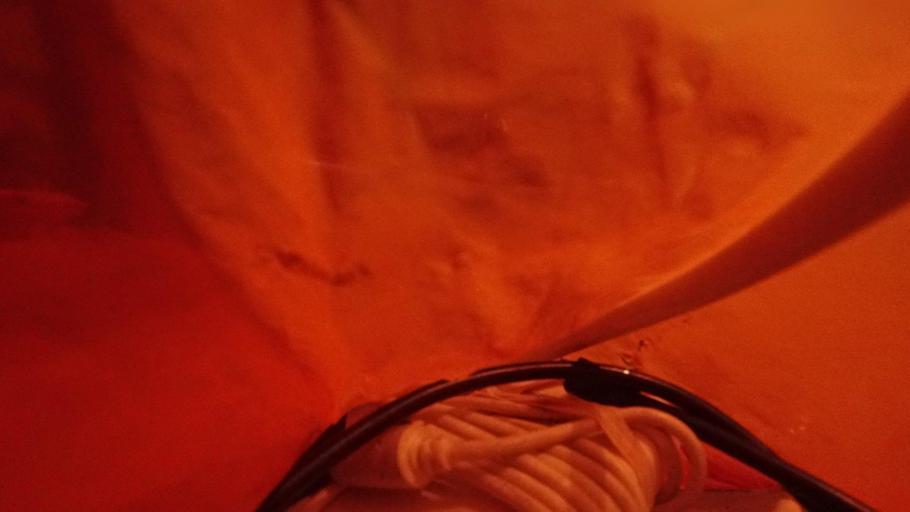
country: RU
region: Jewish Autonomous Oblast
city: Khingansk
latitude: 49.1633
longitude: 130.7672
